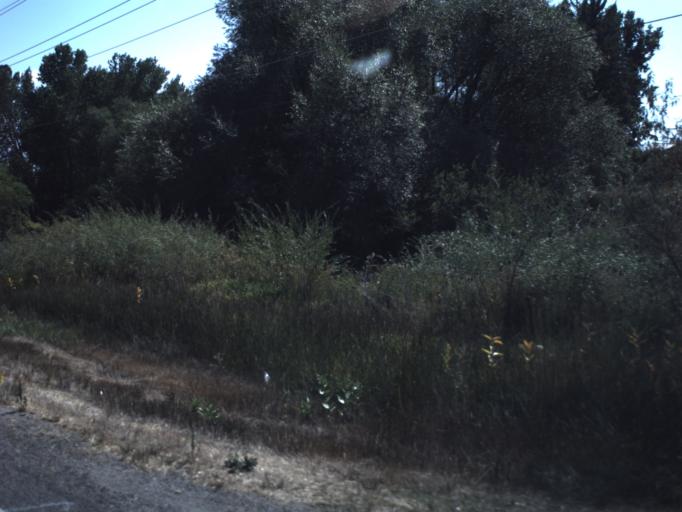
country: US
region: Utah
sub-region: Cache County
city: Smithfield
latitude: 41.8420
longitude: -111.8840
